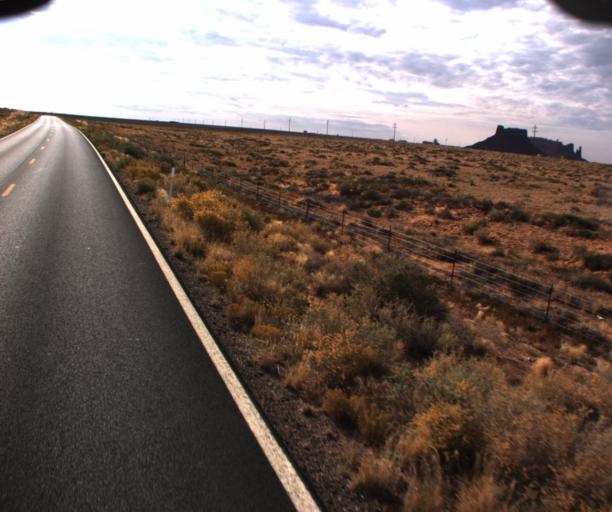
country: US
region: Arizona
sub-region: Apache County
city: Many Farms
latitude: 36.5633
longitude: -109.5421
